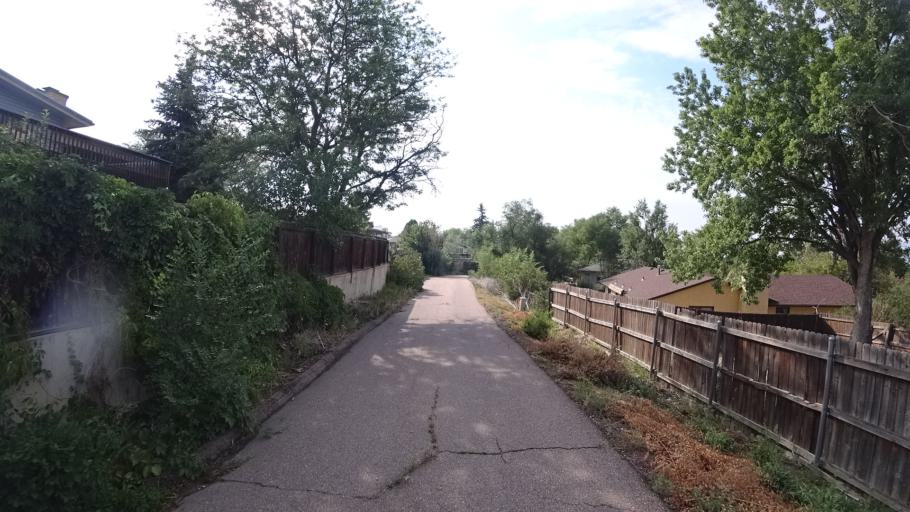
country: US
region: Colorado
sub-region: El Paso County
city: Colorado Springs
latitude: 38.8870
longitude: -104.8014
